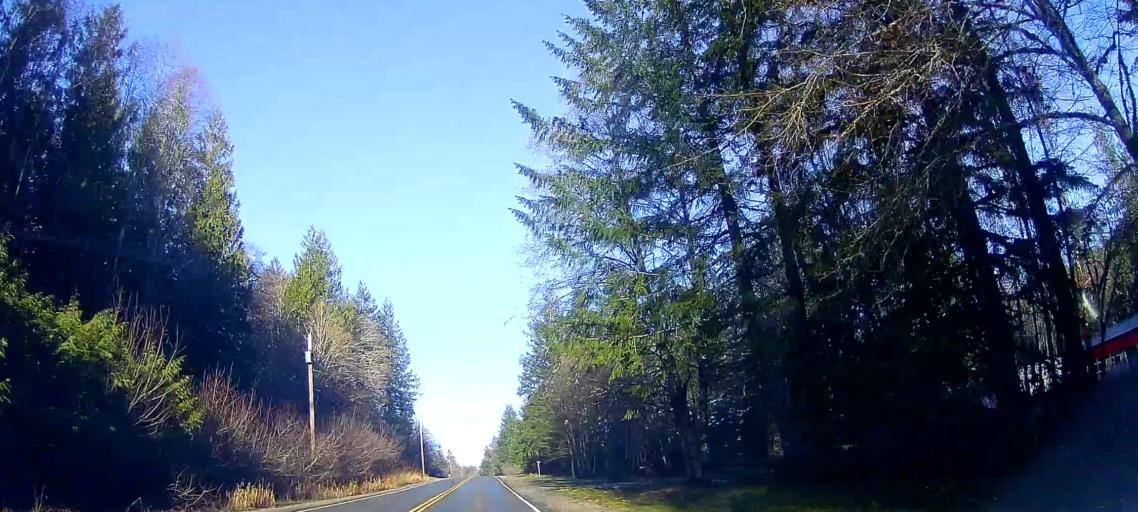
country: US
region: Washington
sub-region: Snohomish County
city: Darrington
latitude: 48.5915
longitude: -121.7722
